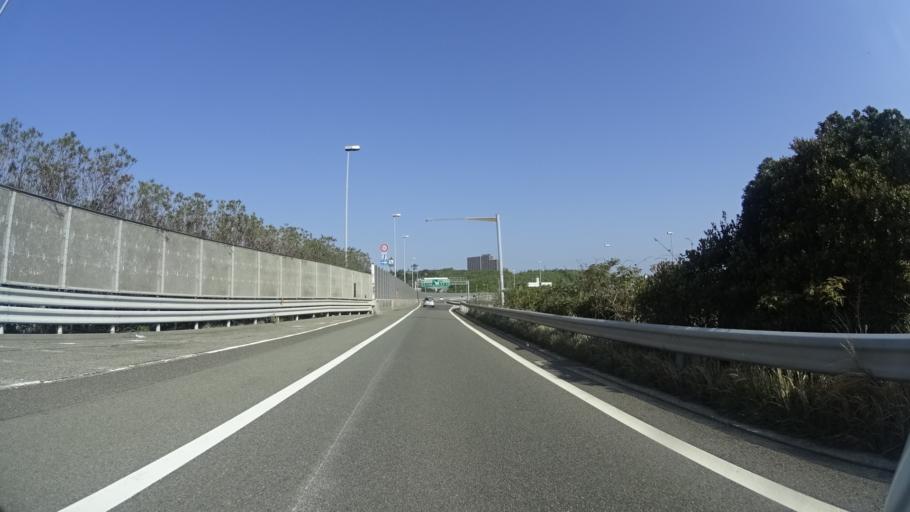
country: JP
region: Hyogo
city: Akashi
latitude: 34.6497
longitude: 135.0717
